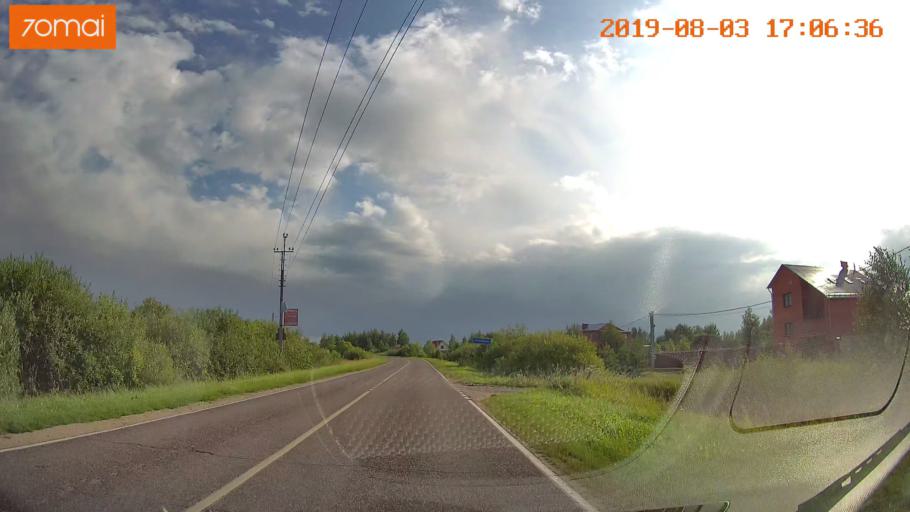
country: RU
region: Moskovskaya
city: Troitskoye
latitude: 55.3060
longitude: 38.5496
